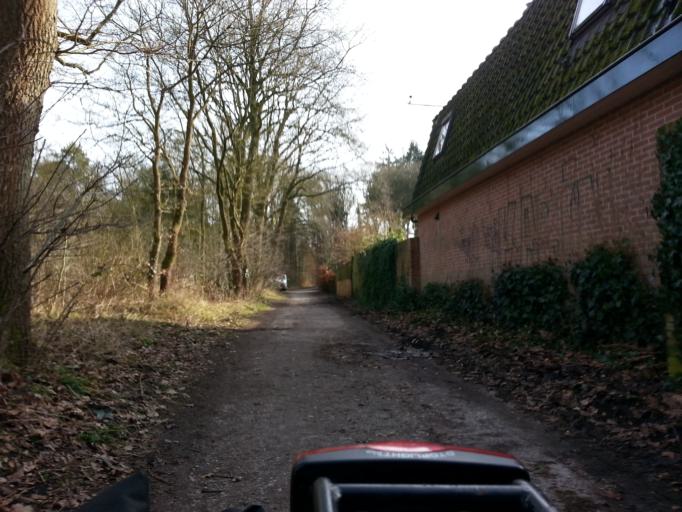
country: NL
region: Utrecht
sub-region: Gemeente Utrechtse Heuvelrug
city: Driebergen-Rijsenburg
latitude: 52.0772
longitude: 5.3184
